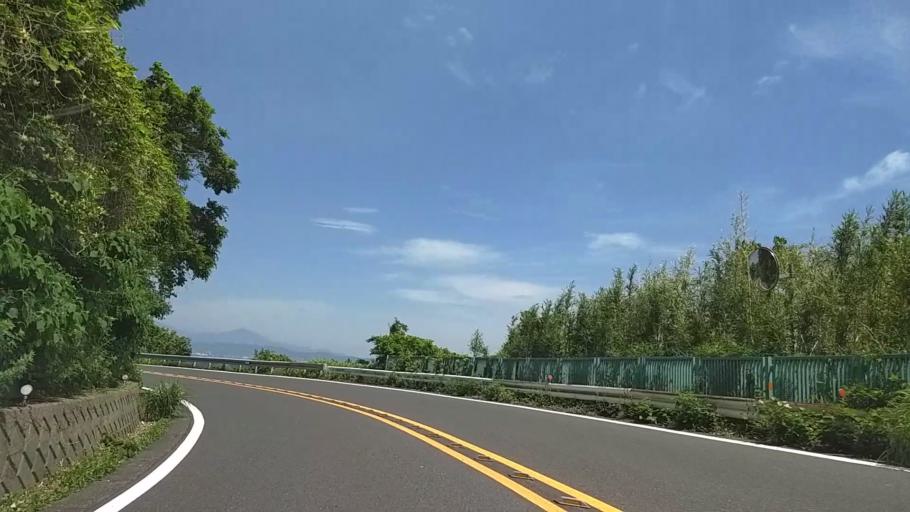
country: JP
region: Kanagawa
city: Yugawara
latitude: 35.1675
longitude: 139.1444
